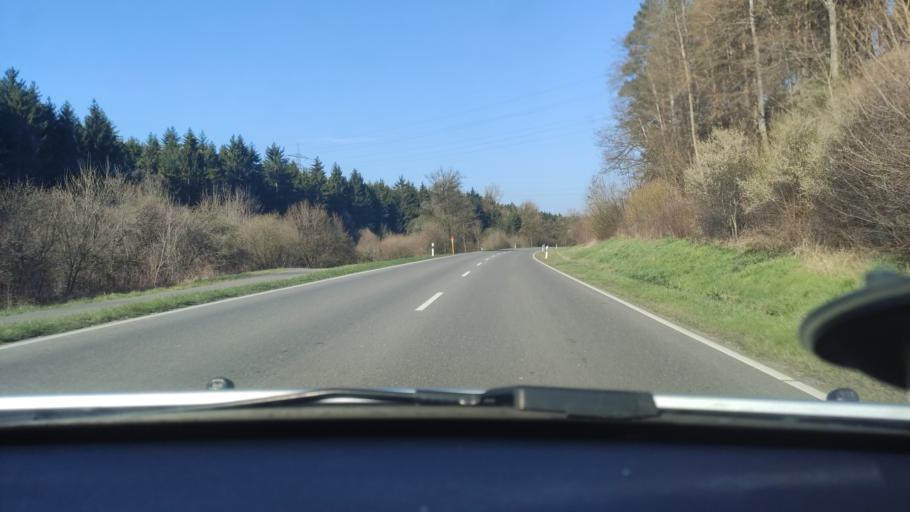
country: DE
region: Baden-Wuerttemberg
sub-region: Tuebingen Region
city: Grosselfingen
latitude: 48.3139
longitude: 8.8799
